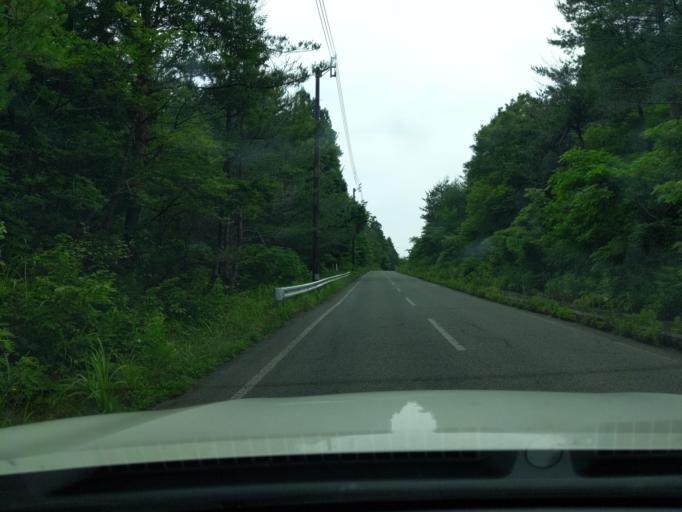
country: JP
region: Niigata
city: Kashiwazaki
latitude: 37.3341
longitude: 138.5842
